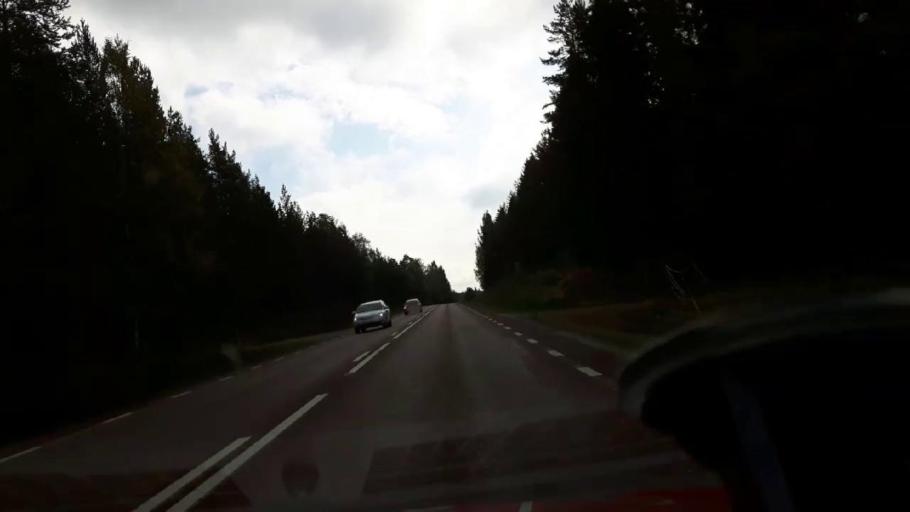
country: SE
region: Gaevleborg
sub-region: Bollnas Kommun
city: Kilafors
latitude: 61.2655
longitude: 16.5475
